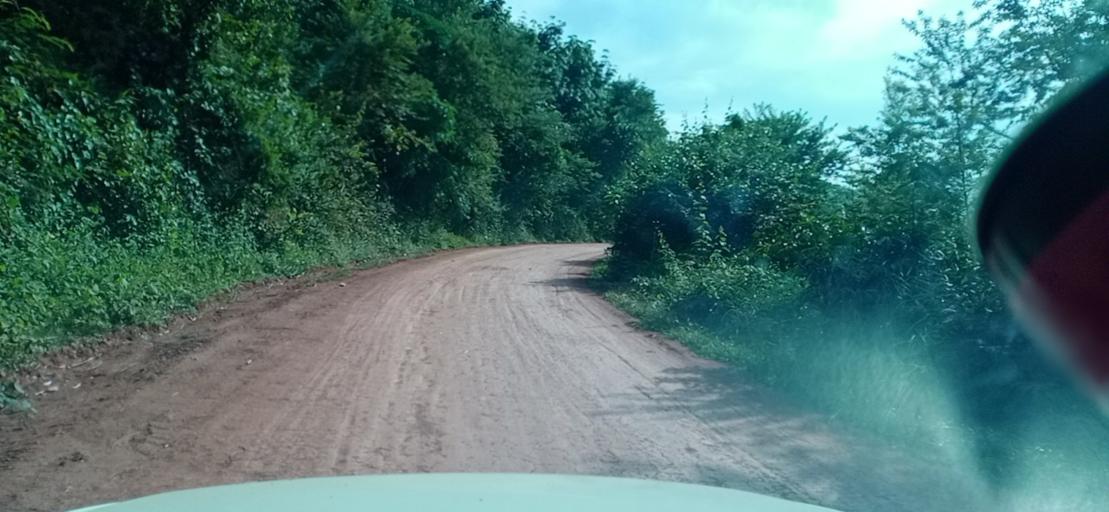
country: TH
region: Changwat Bueng Kan
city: Pak Khat
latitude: 18.6698
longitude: 103.1971
